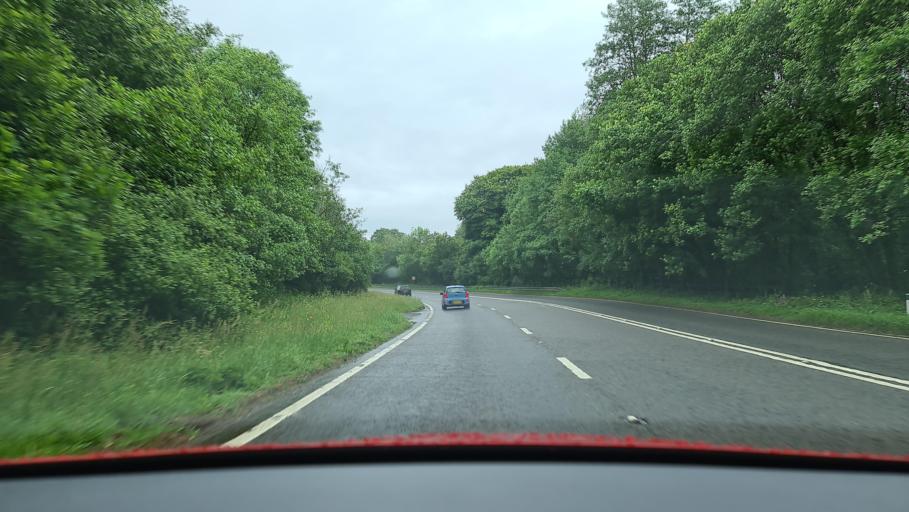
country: GB
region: England
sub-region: Cornwall
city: Liskeard
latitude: 50.4573
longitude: -4.5466
